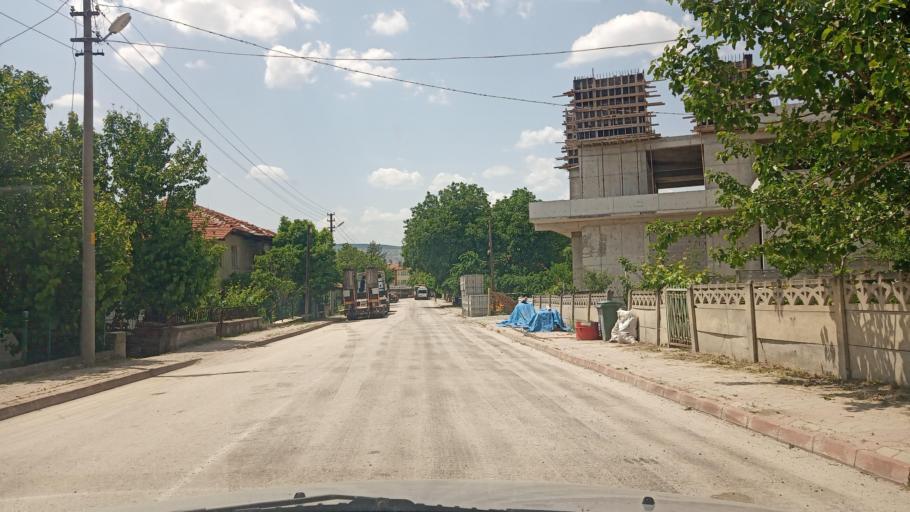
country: TR
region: Bolu
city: Seben
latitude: 40.4083
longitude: 31.5750
